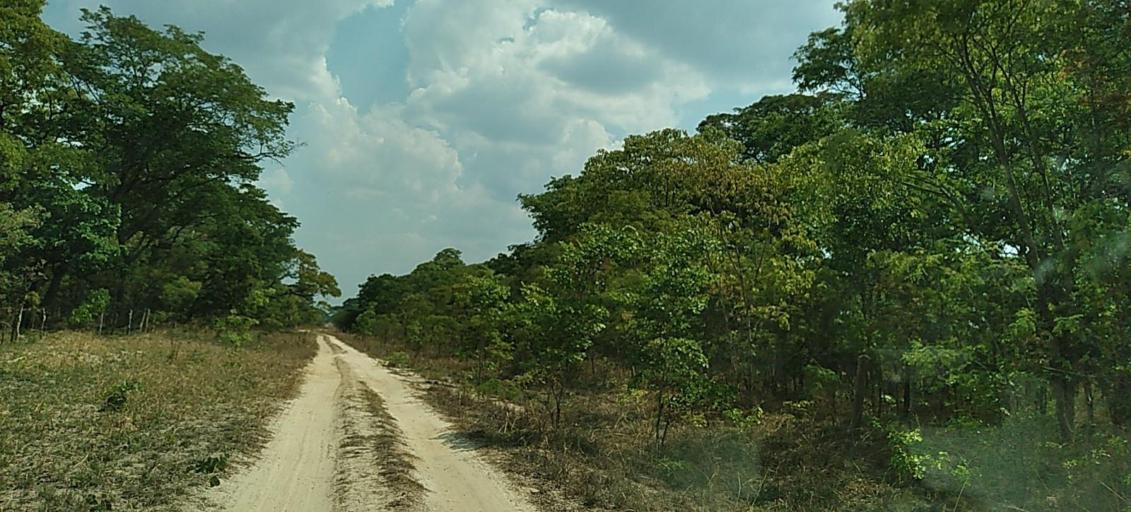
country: ZM
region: Copperbelt
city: Mpongwe
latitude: -13.8299
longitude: 27.9402
